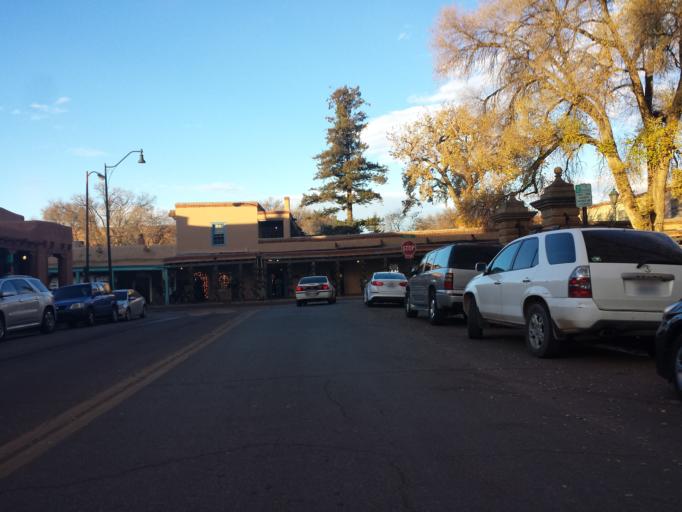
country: US
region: New Mexico
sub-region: Santa Fe County
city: Santa Fe
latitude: 35.6869
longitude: -105.9368
